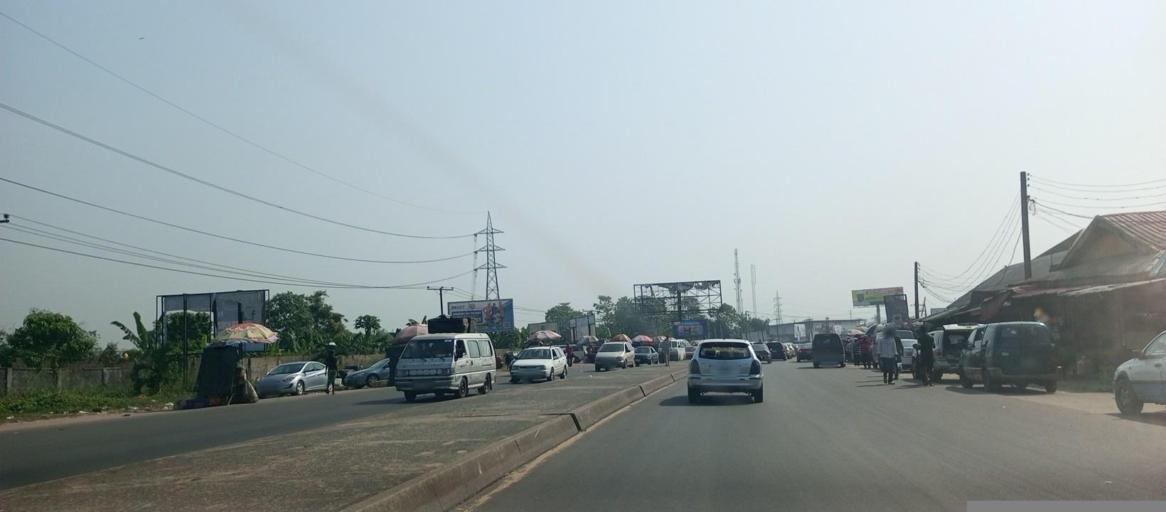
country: NG
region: Rivers
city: Emuoha
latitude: 4.8989
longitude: 6.9046
